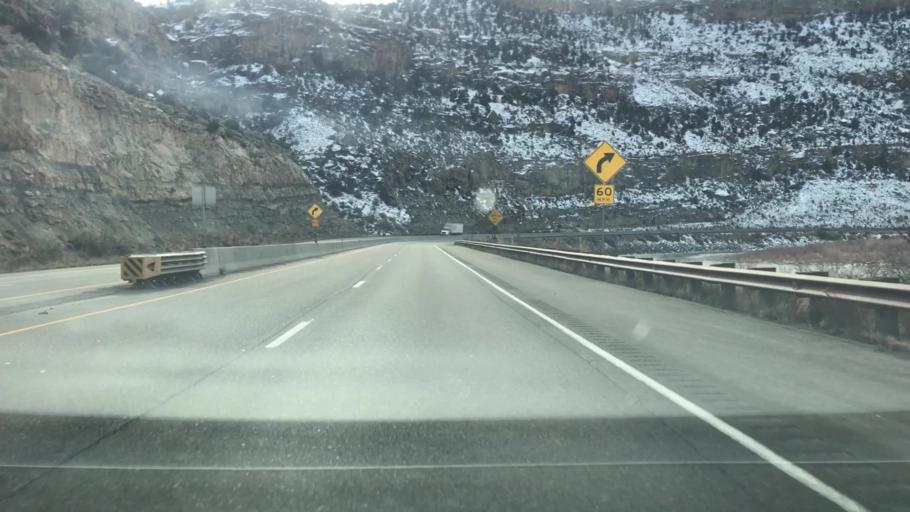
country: US
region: Colorado
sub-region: Mesa County
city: Palisade
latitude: 39.2431
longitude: -108.2556
